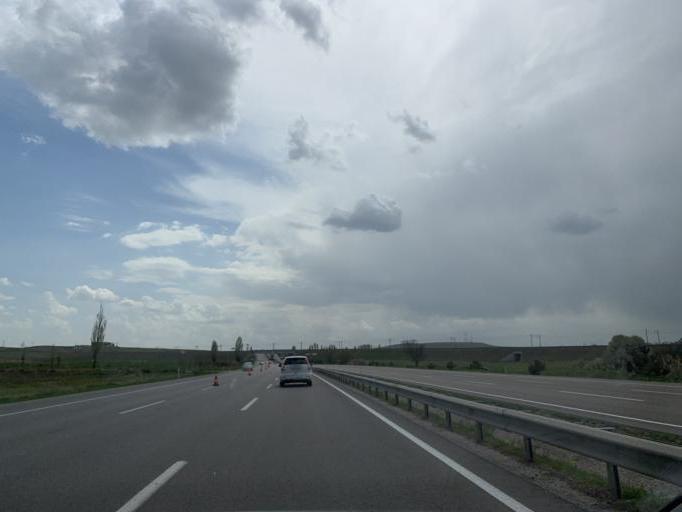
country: TR
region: Ankara
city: Polatli
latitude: 39.6290
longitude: 32.1952
